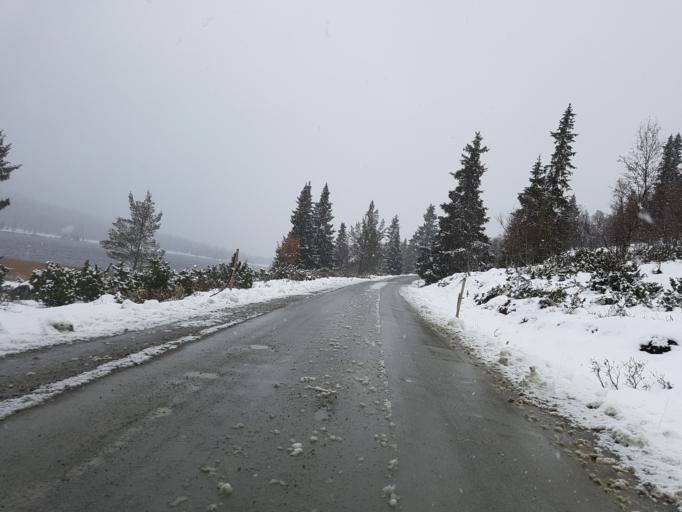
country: NO
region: Oppland
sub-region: Sel
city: Otta
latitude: 61.7938
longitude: 9.7162
